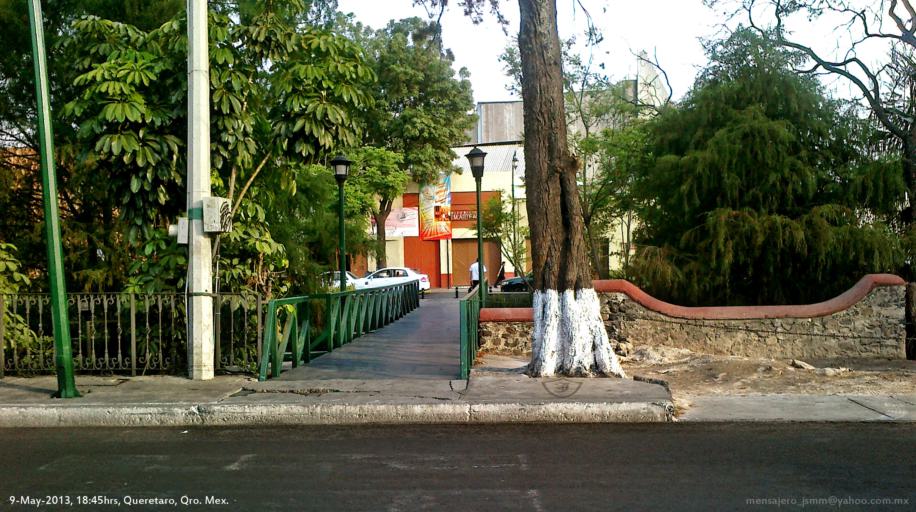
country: MX
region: Queretaro
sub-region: Queretaro
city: Santiago de Queretaro
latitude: 20.5983
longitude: -100.3952
